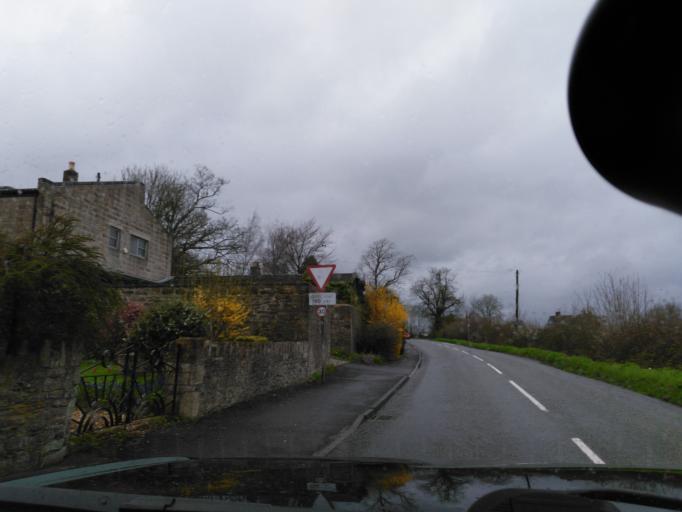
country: GB
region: England
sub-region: Wiltshire
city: Wingfield
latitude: 51.2843
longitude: -2.2743
